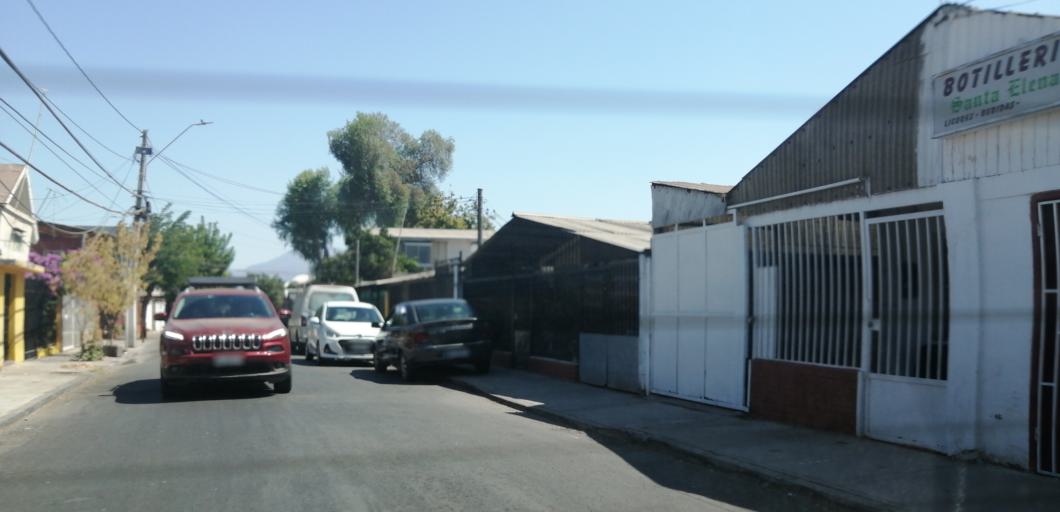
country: CL
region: Santiago Metropolitan
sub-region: Provincia de Santiago
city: Lo Prado
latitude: -33.4337
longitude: -70.7434
